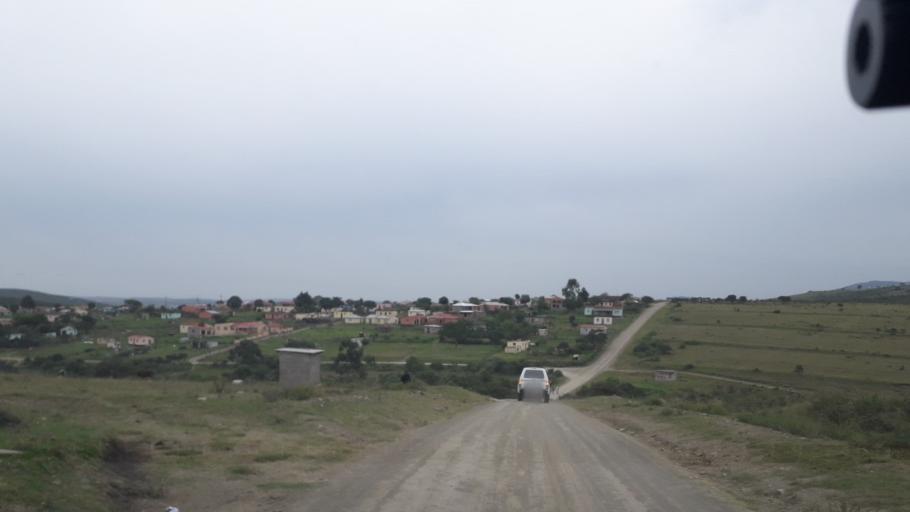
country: ZA
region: Eastern Cape
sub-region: Buffalo City Metropolitan Municipality
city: Bhisho
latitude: -32.7959
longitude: 27.3445
